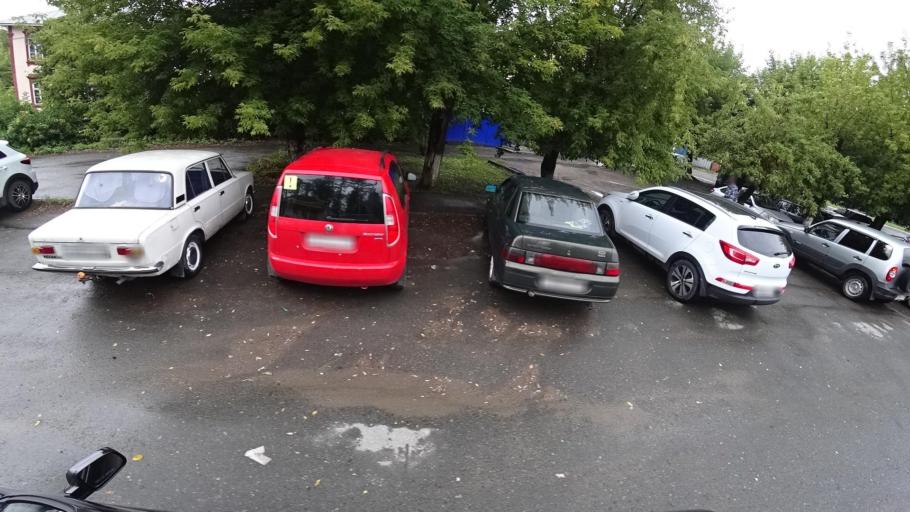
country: RU
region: Sverdlovsk
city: Kamyshlov
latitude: 56.8484
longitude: 62.7119
